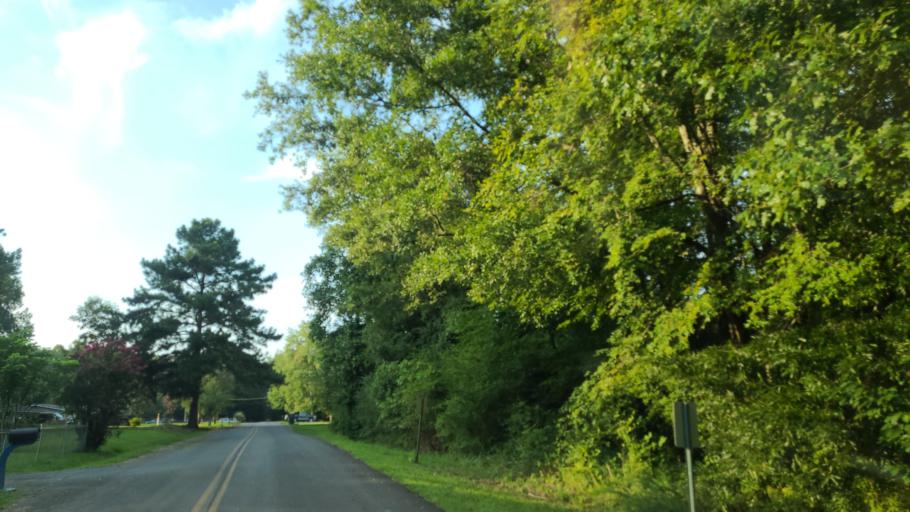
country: US
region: Georgia
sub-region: Whitfield County
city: Dalton
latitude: 34.6864
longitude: -84.9816
